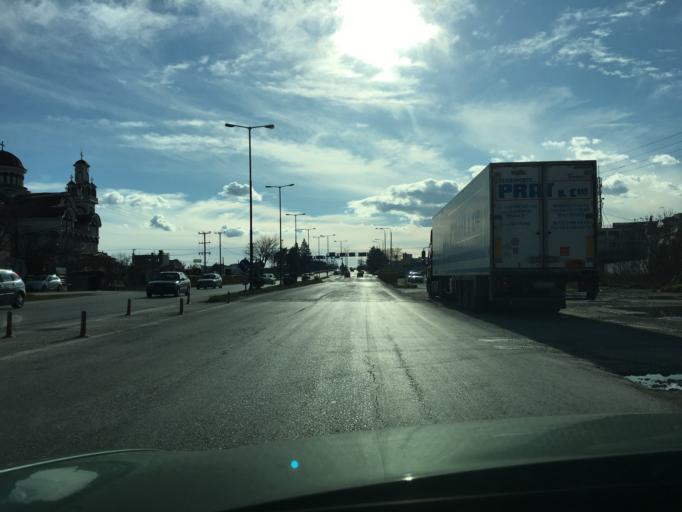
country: GR
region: Thessaly
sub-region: Nomos Larisis
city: Larisa
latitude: 39.6351
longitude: 22.4356
